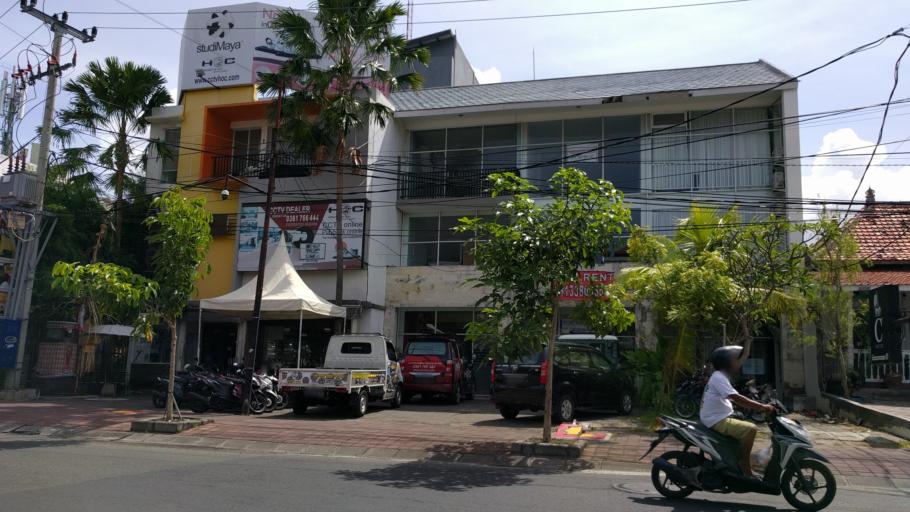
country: ID
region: Bali
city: Kuta
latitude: -8.7032
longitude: 115.1761
